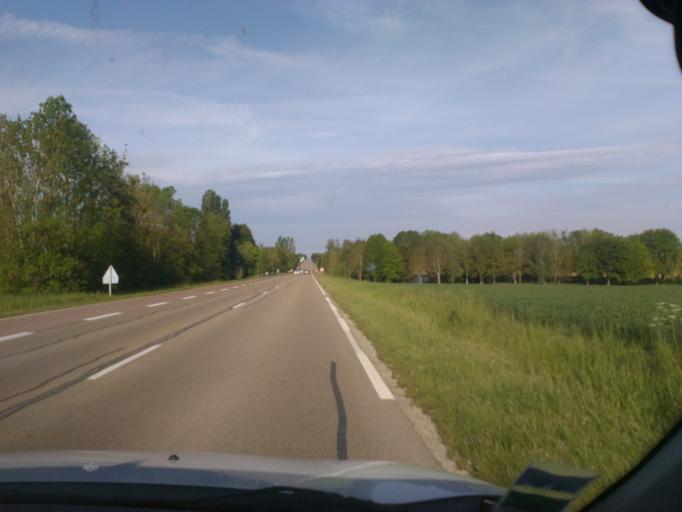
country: FR
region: Champagne-Ardenne
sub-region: Departement de l'Aube
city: Lusigny-sur-Barse
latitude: 48.2414
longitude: 4.3322
